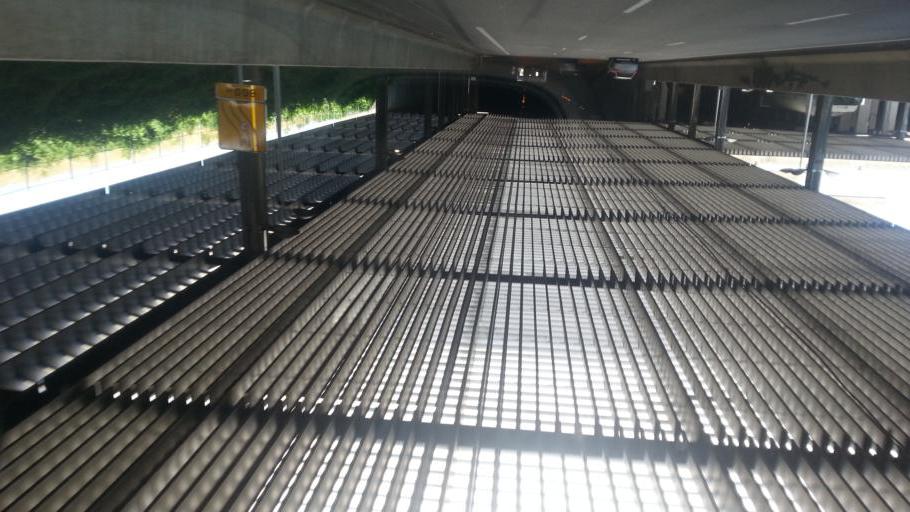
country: FR
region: Ile-de-France
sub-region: Departement du Val-d'Oise
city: Roissy-en-France
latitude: 49.0194
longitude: 2.5335
